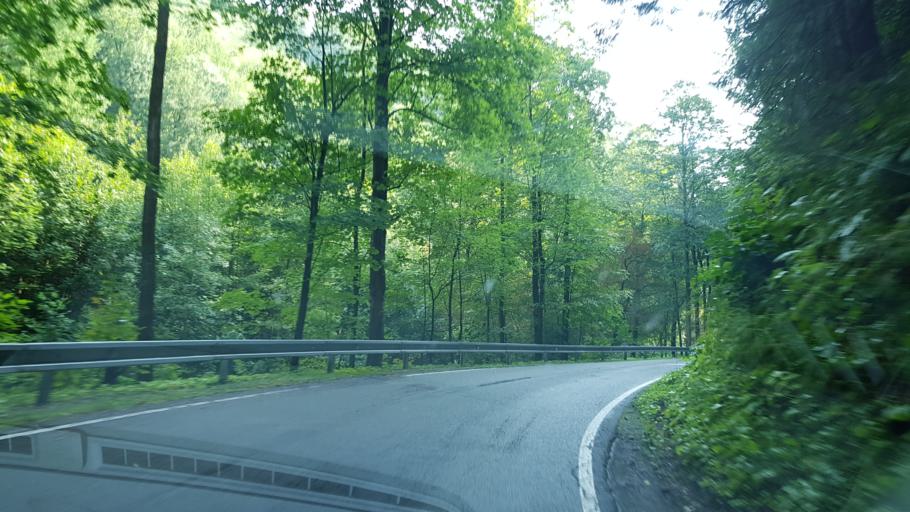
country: CZ
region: Olomoucky
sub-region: Okres Jesenik
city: Jesenik
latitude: 50.2082
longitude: 17.2461
